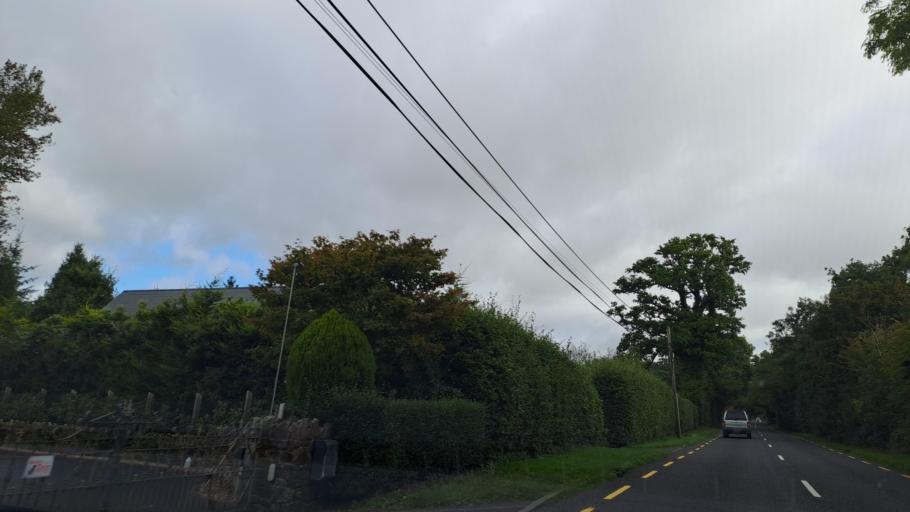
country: IE
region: Ulster
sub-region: County Monaghan
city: Carrickmacross
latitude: 53.9643
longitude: -6.7442
